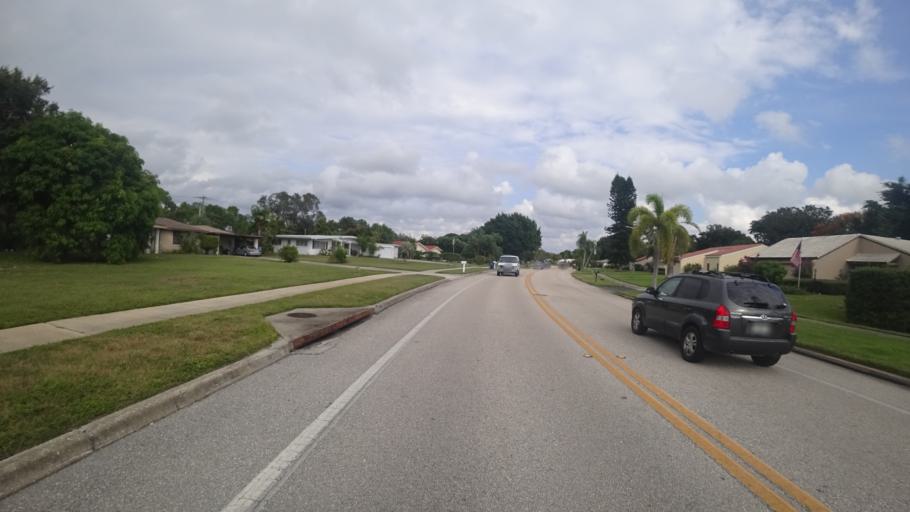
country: US
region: Florida
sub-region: Manatee County
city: Whitfield
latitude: 27.4139
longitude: -82.5664
